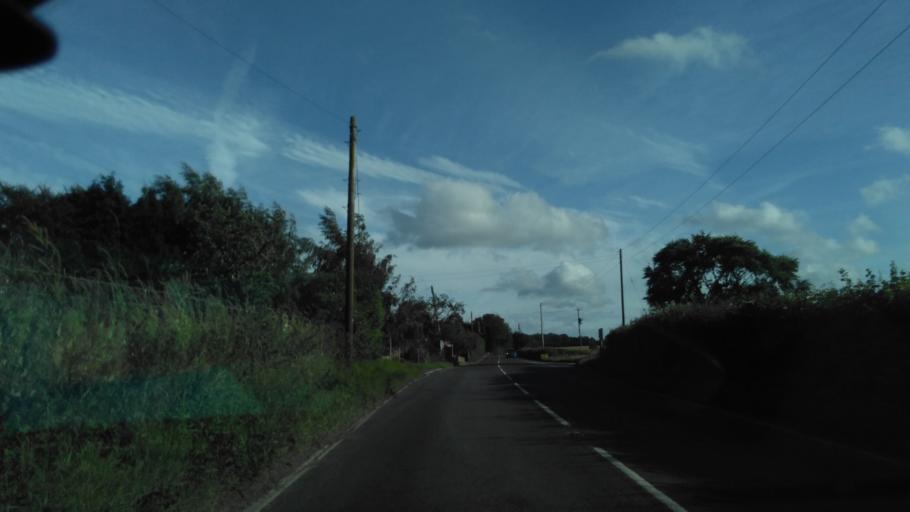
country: GB
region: England
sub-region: Kent
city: Faversham
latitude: 51.2425
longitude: 0.8773
